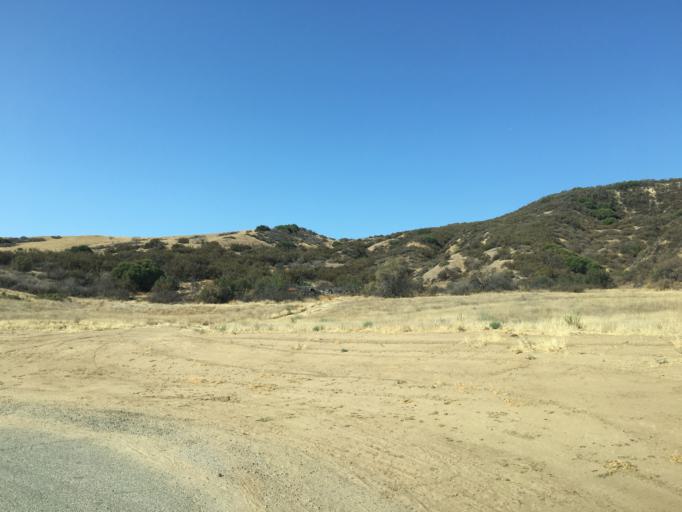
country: US
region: California
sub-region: Los Angeles County
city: Val Verde
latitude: 34.4581
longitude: -118.6473
